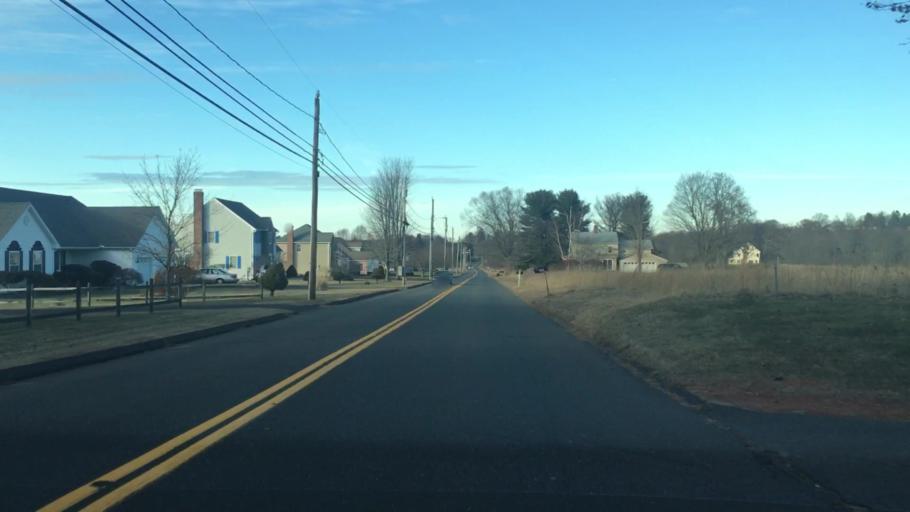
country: US
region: Connecticut
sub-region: Middlesex County
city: Middletown
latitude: 41.5226
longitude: -72.6494
